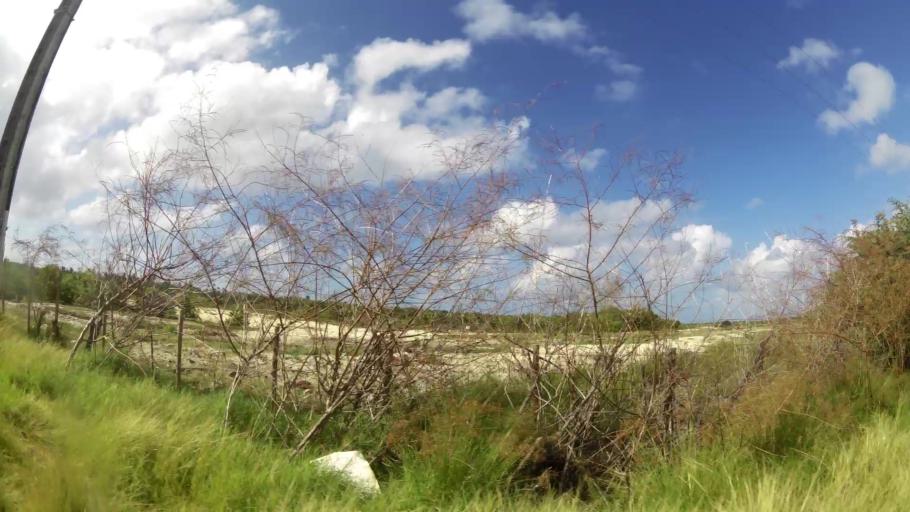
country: MQ
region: Martinique
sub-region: Martinique
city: Le Marin
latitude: 14.4069
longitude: -60.8758
